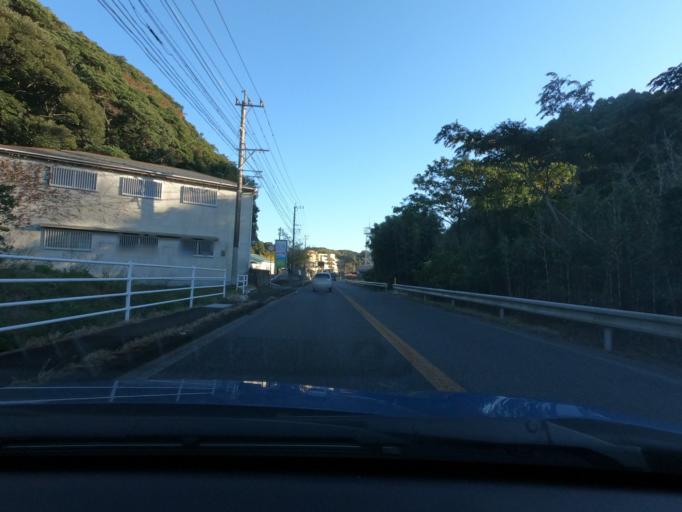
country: JP
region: Kagoshima
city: Satsumasendai
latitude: 31.8620
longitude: 130.2271
